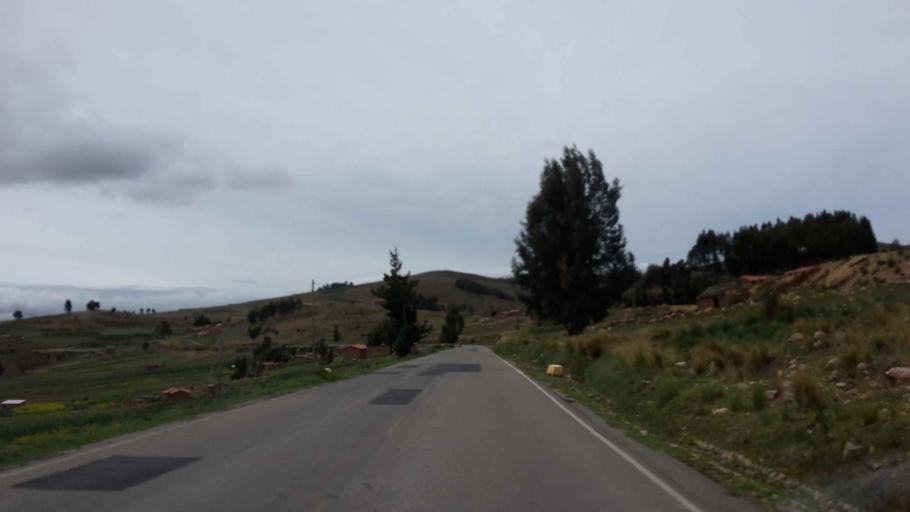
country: BO
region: Cochabamba
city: Arani
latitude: -17.4709
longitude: -65.6525
